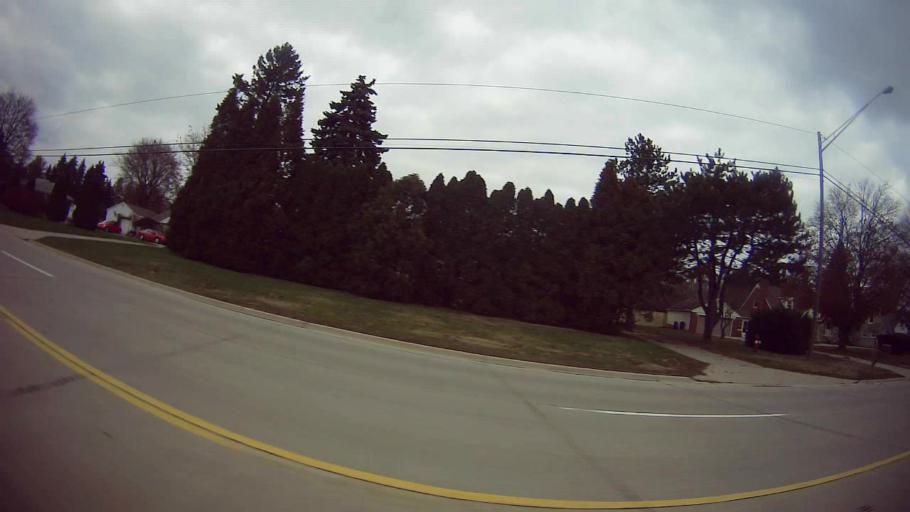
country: US
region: Michigan
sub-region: Macomb County
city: Fraser
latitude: 42.5529
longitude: -82.9751
